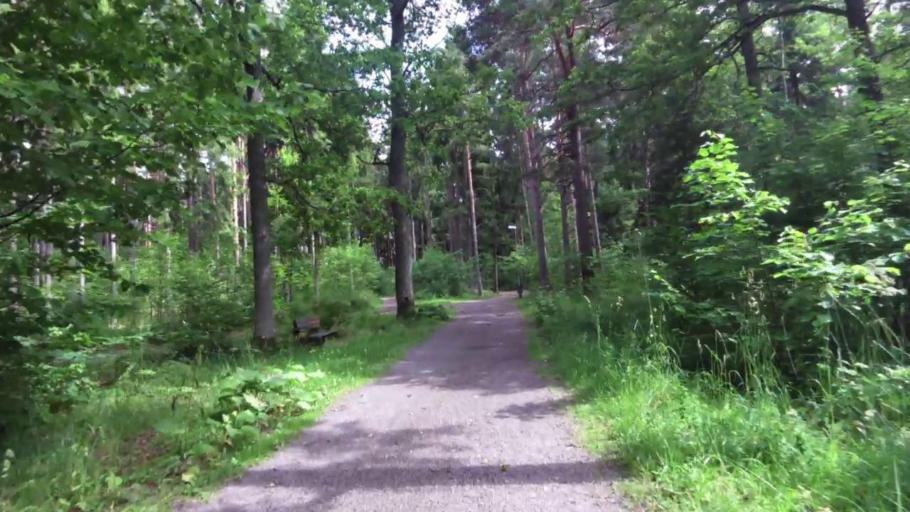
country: SE
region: OEstergoetland
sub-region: Linkopings Kommun
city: Linkoping
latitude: 58.4197
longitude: 15.5767
